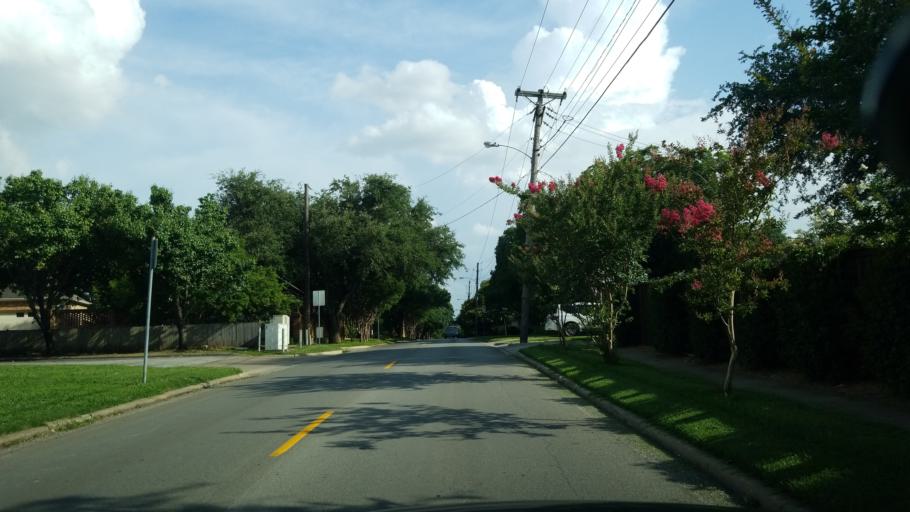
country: US
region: Texas
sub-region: Dallas County
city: University Park
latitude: 32.8622
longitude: -96.7768
